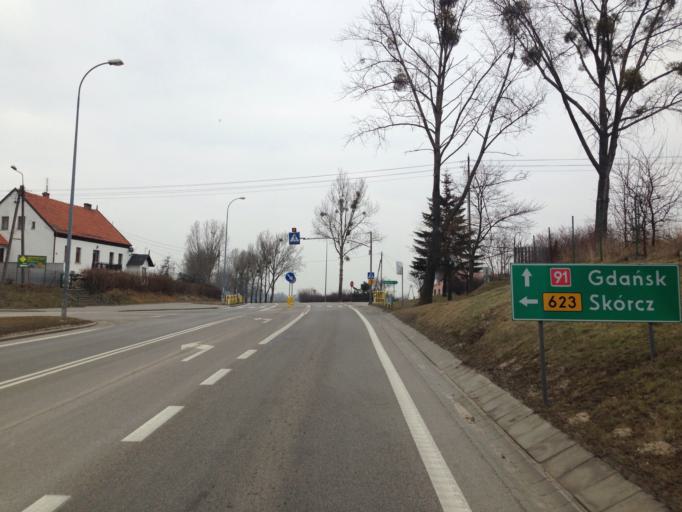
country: PL
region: Pomeranian Voivodeship
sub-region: Powiat starogardzki
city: Smetowo Graniczne
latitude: 53.7662
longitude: 18.7676
